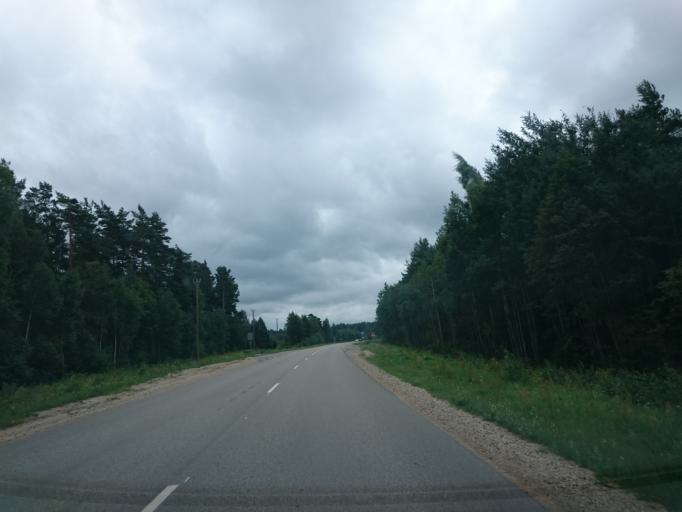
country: LV
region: Pavilostas
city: Pavilosta
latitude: 56.7733
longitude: 21.2559
